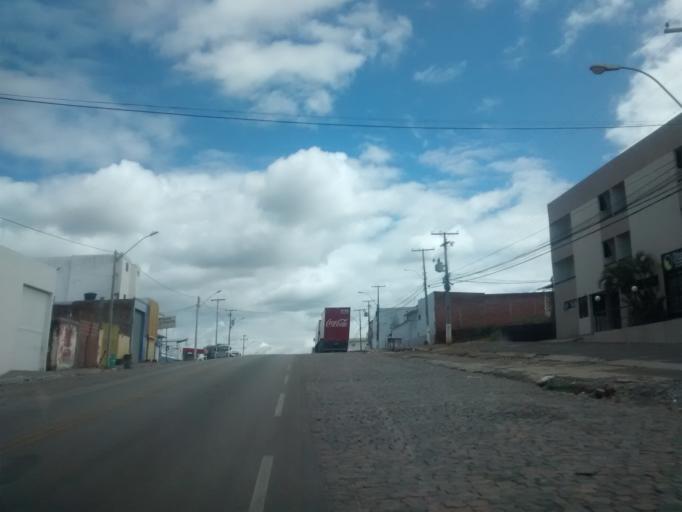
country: BR
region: Bahia
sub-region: Brumado
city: Brumado
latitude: -14.2164
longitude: -41.6823
